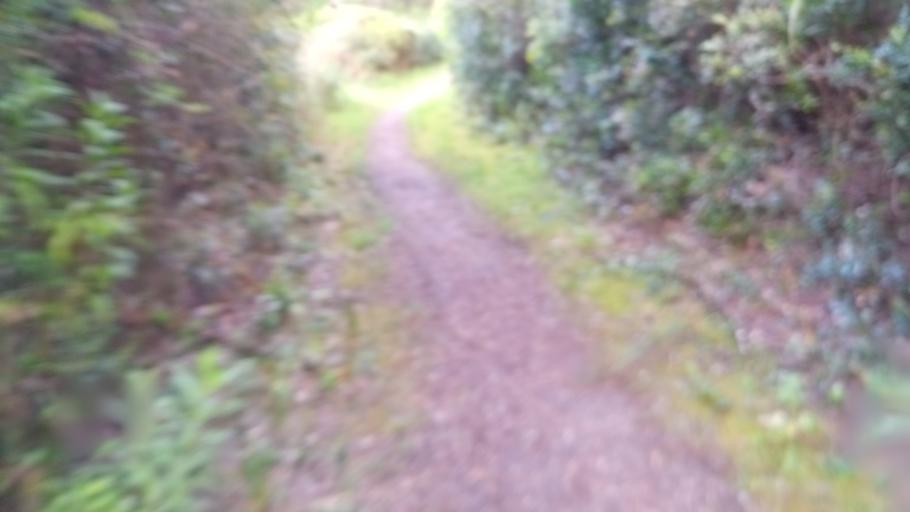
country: PT
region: Leiria
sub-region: Caldas da Rainha
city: Caldas da Rainha
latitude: 39.4017
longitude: -9.1897
